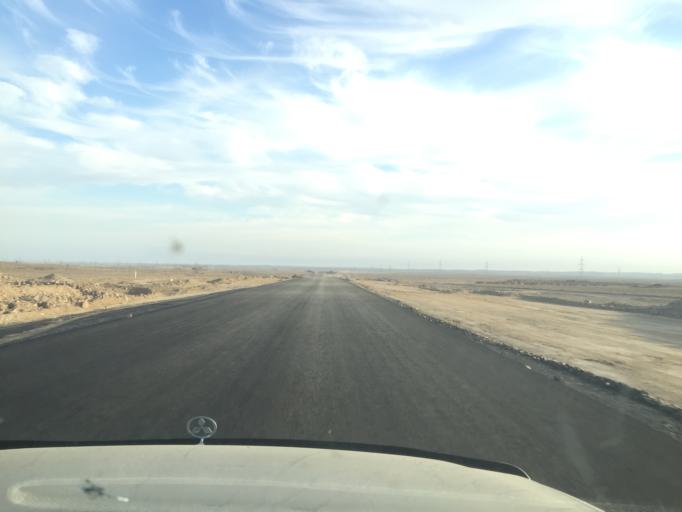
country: KZ
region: Almaty Oblysy
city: Ulken
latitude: 45.2629
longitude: 73.7983
